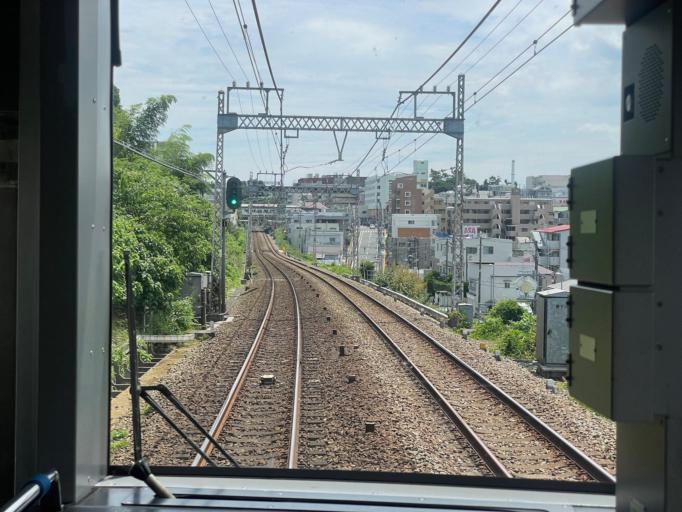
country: JP
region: Kanagawa
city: Fujisawa
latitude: 35.3666
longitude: 139.4728
